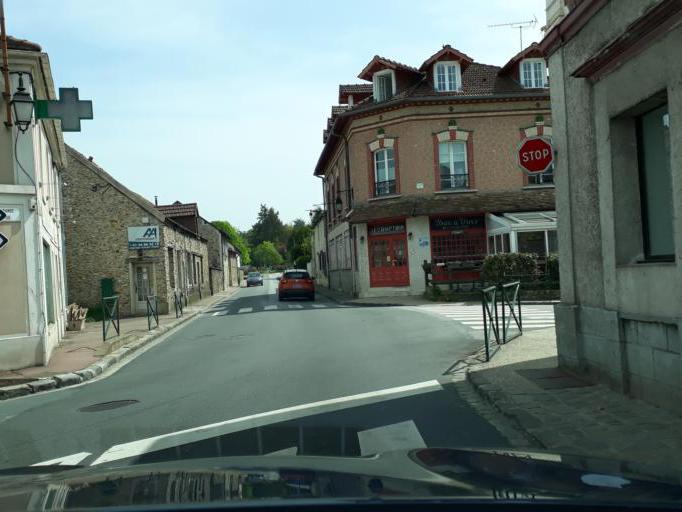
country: FR
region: Ile-de-France
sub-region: Departement des Yvelines
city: Saint-Leger-en-Yvelines
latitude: 48.7209
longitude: 1.7664
